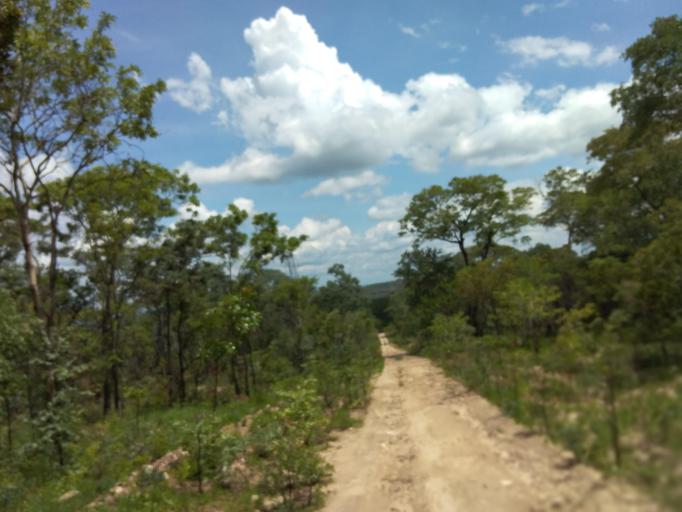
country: ZM
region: Central
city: Mkushi
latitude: -14.0800
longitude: 29.9711
